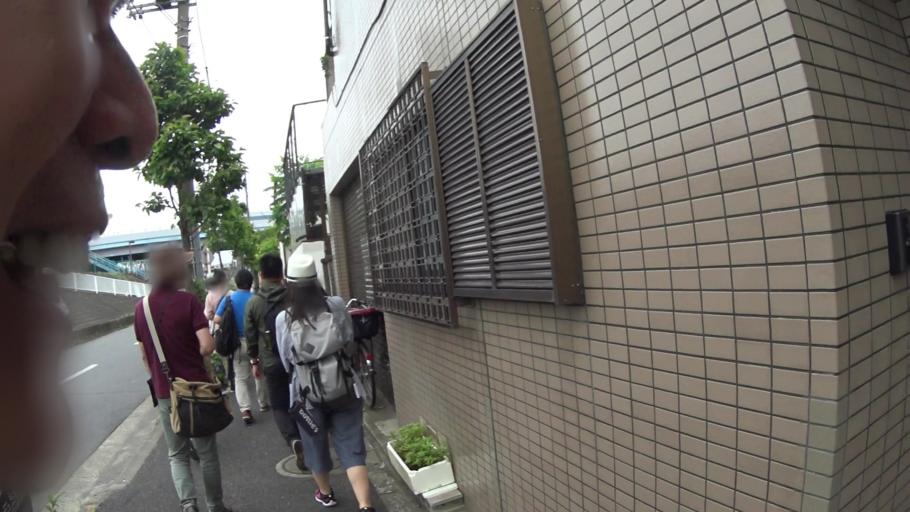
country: JP
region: Tokyo
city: Urayasu
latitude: 35.7120
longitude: 139.8455
